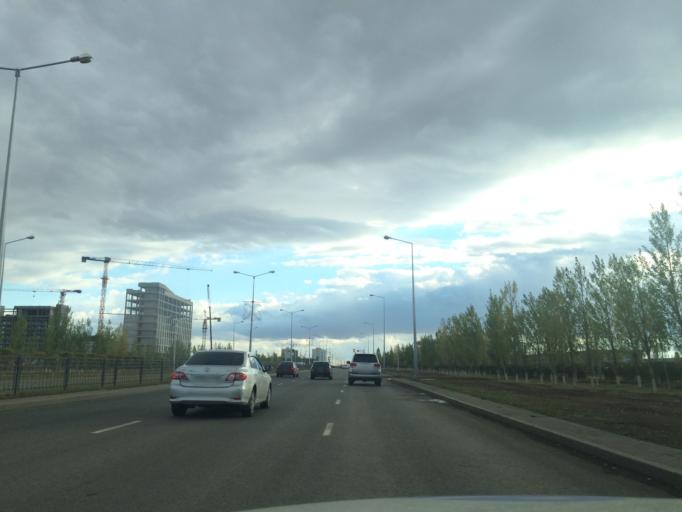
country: KZ
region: Astana Qalasy
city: Astana
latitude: 51.1165
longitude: 71.4006
